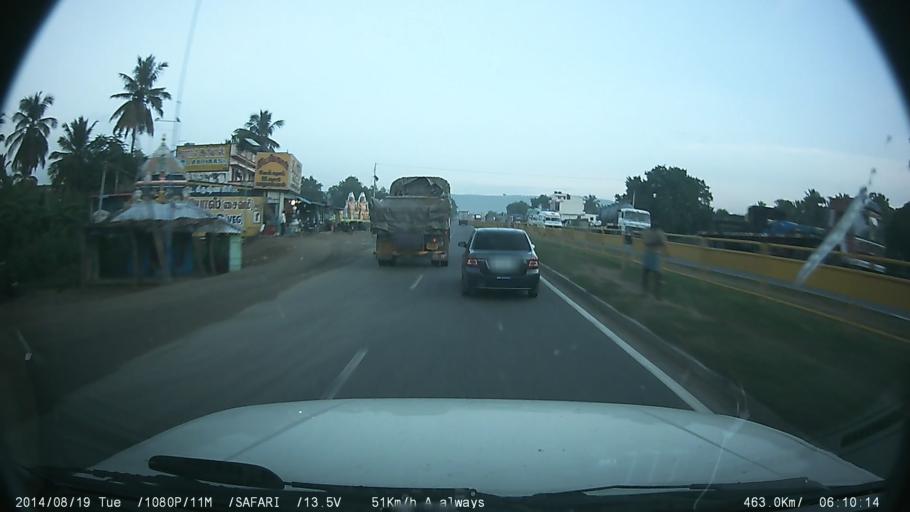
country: IN
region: Tamil Nadu
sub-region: Salem
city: Omalur
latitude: 11.9394
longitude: 78.0517
